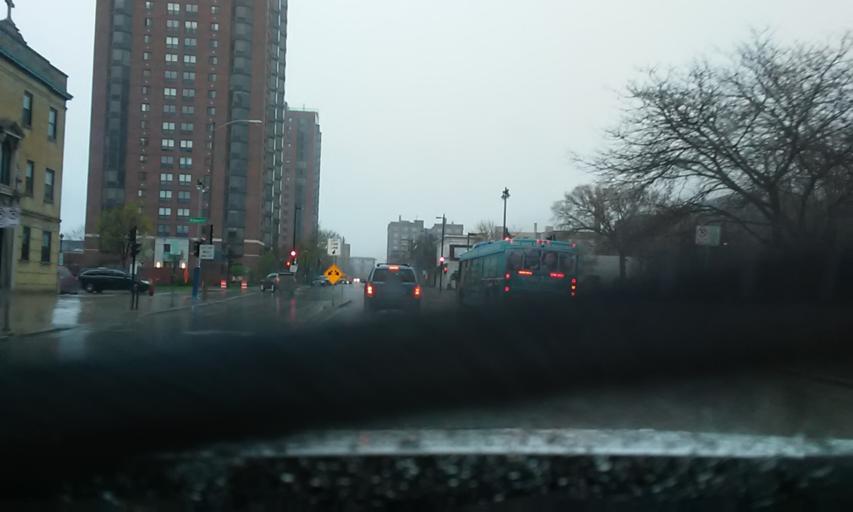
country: US
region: Wisconsin
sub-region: Milwaukee County
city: Milwaukee
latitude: 43.0421
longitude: -87.9031
